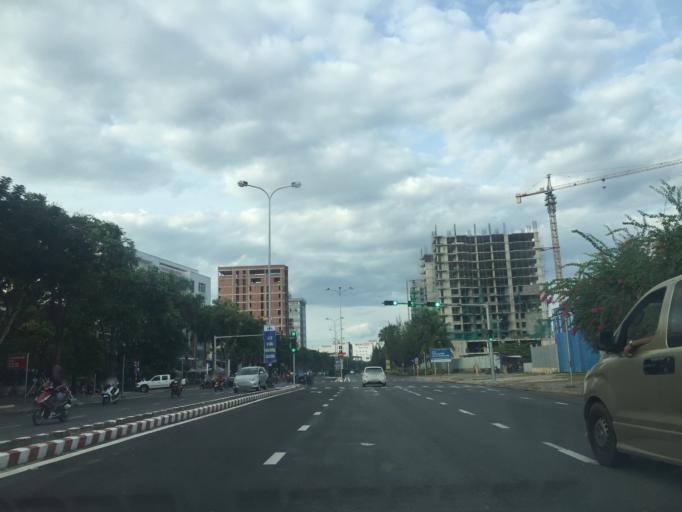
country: VN
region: Da Nang
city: Da Nang
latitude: 16.0809
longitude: 108.2113
